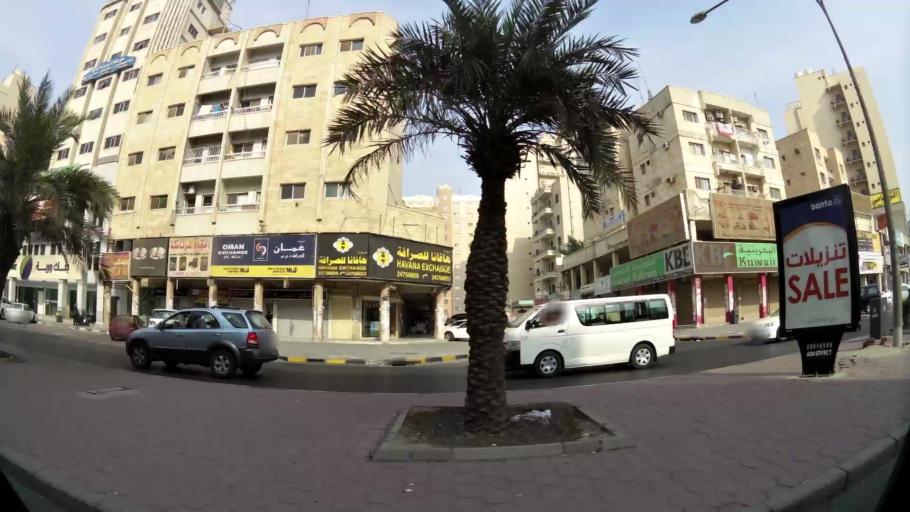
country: KW
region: Al Farwaniyah
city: Al Farwaniyah
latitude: 29.2735
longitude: 47.9645
